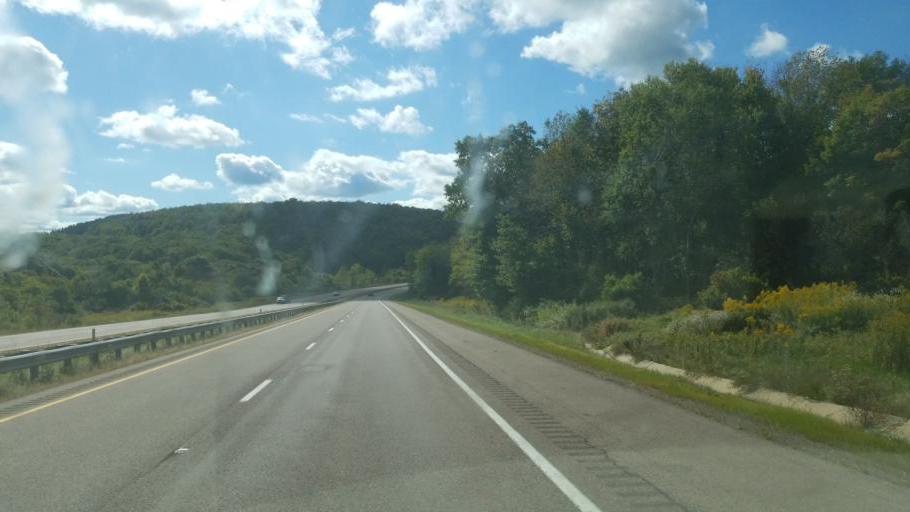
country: US
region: Maryland
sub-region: Garrett County
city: Oakland
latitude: 39.6990
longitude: -79.3170
